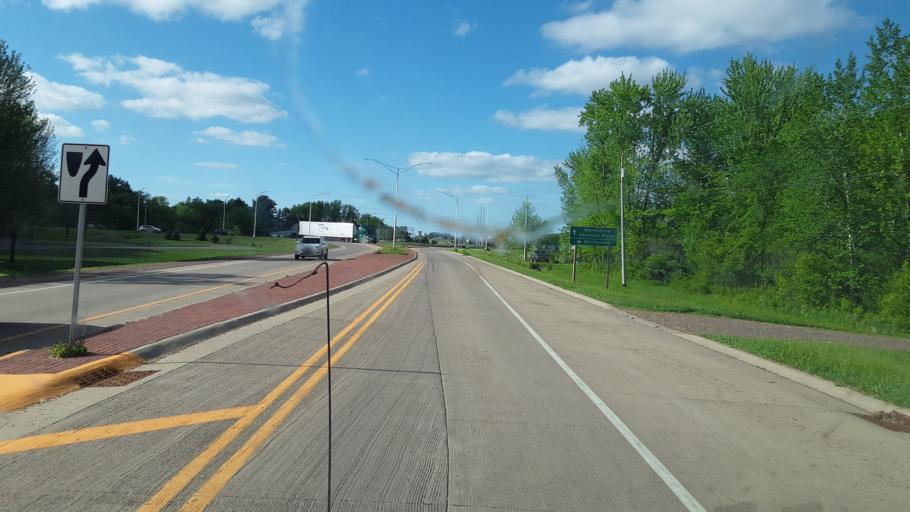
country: US
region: Wisconsin
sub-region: Wood County
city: Marshfield
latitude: 44.5964
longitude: -90.1805
